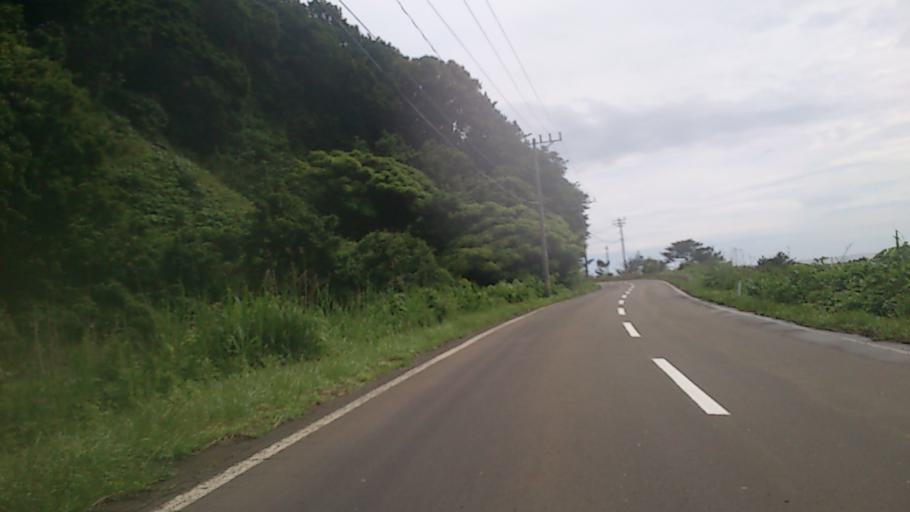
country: JP
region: Akita
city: Noshiromachi
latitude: 40.4696
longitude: 139.9465
